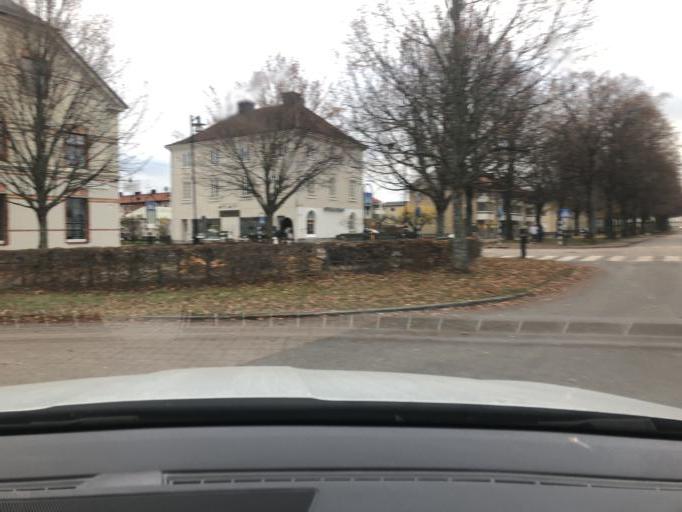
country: SE
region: Uppsala
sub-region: Tierps Kommun
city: Tierp
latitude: 60.3438
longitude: 17.5154
